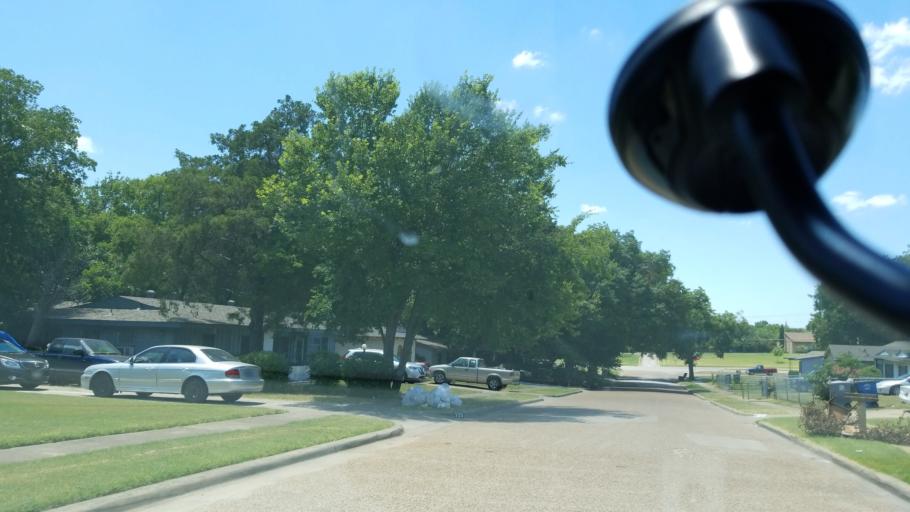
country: US
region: Texas
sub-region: Dallas County
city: Cockrell Hill
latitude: 32.6893
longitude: -96.8131
